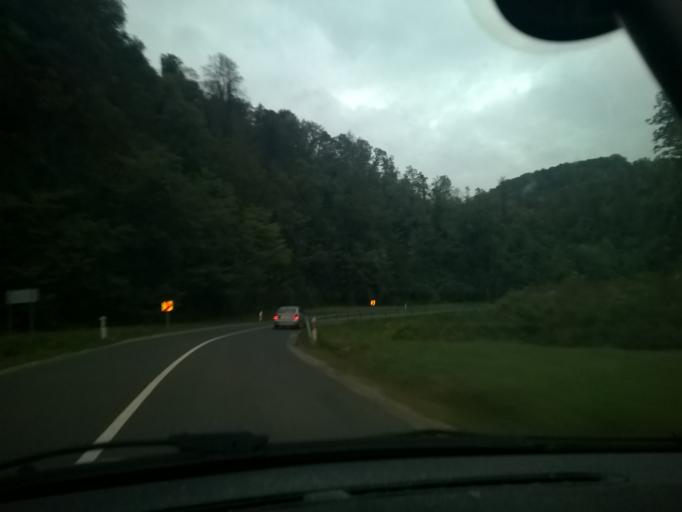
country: HR
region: Krapinsko-Zagorska
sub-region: Grad Krapina
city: Krapina
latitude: 46.1837
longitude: 15.8482
